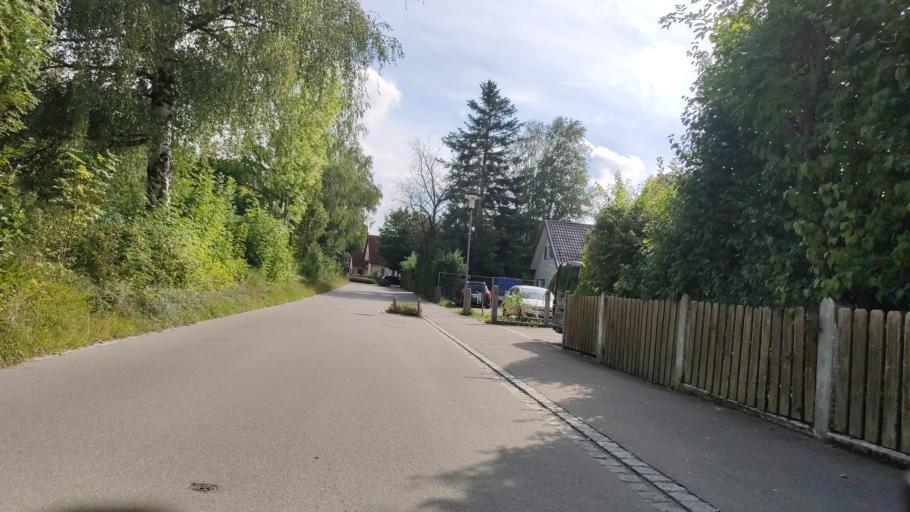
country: DE
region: Bavaria
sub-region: Swabia
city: Klosterlechfeld
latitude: 48.1535
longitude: 10.8318
